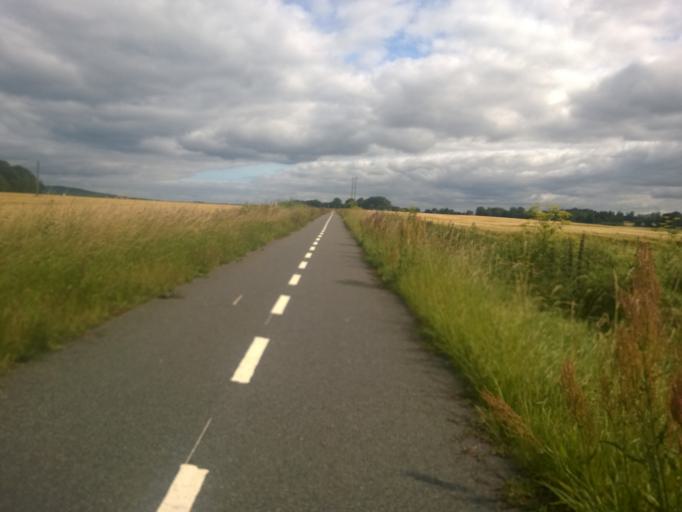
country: SE
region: Skane
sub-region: Kristianstads Kommun
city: Kristianstad
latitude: 56.0672
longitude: 14.1928
